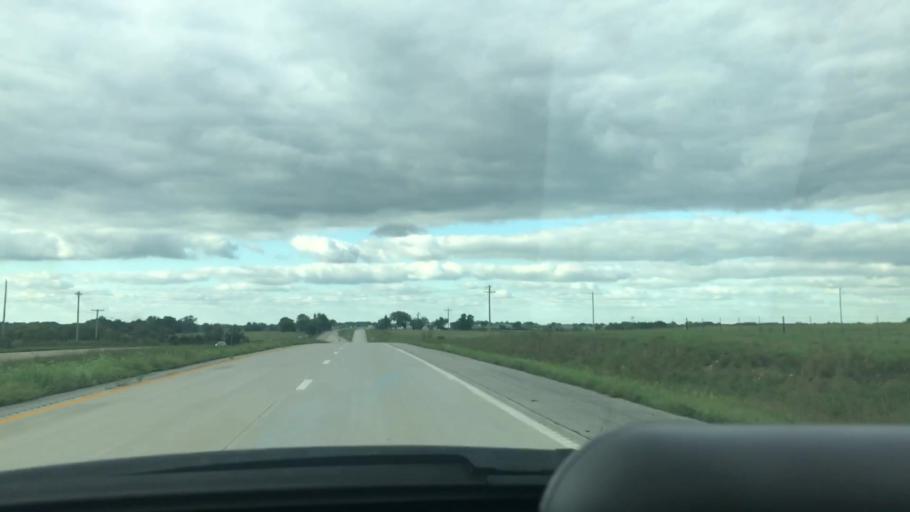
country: US
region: Missouri
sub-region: Benton County
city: Lincoln
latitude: 38.3605
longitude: -93.3391
